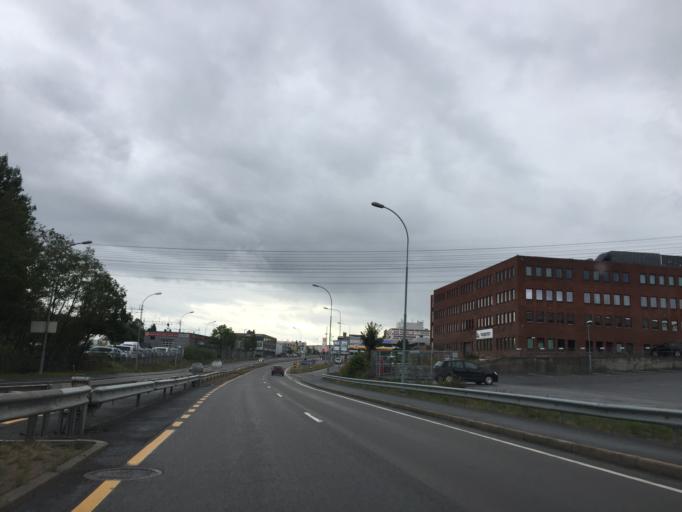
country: NO
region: Akershus
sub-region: Lorenskog
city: Kjenn
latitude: 59.9483
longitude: 10.8818
